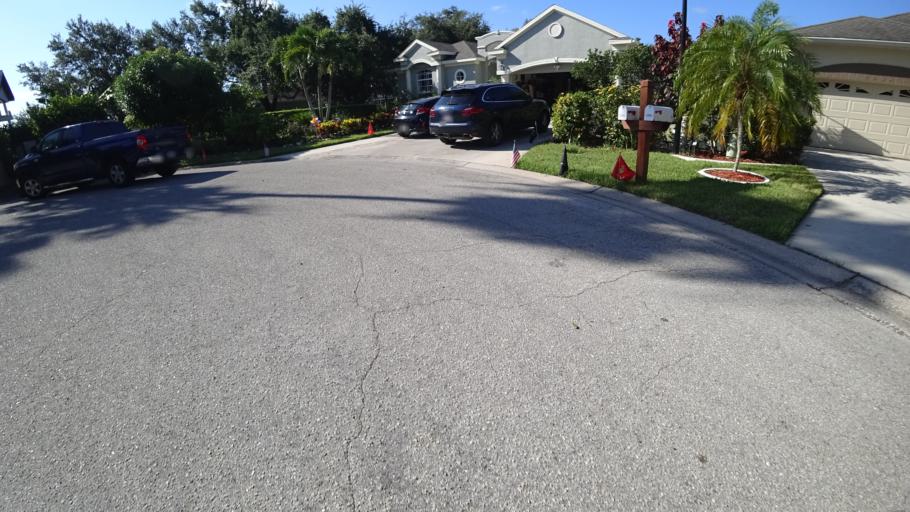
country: US
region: Florida
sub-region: Manatee County
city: Ellenton
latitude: 27.5049
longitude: -82.5163
